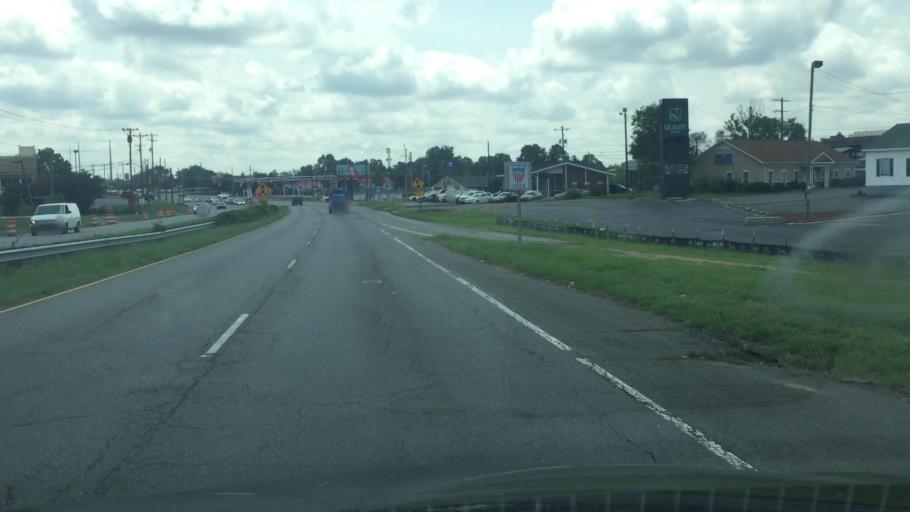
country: US
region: North Carolina
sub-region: Cabarrus County
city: Concord
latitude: 35.4438
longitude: -80.6090
